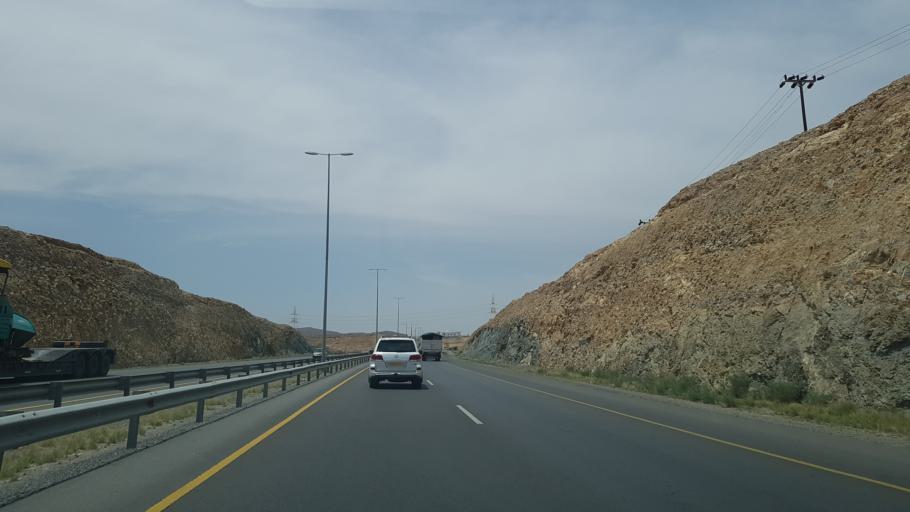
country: OM
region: Muhafazat ad Dakhiliyah
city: Izki
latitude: 22.9131
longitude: 57.7629
